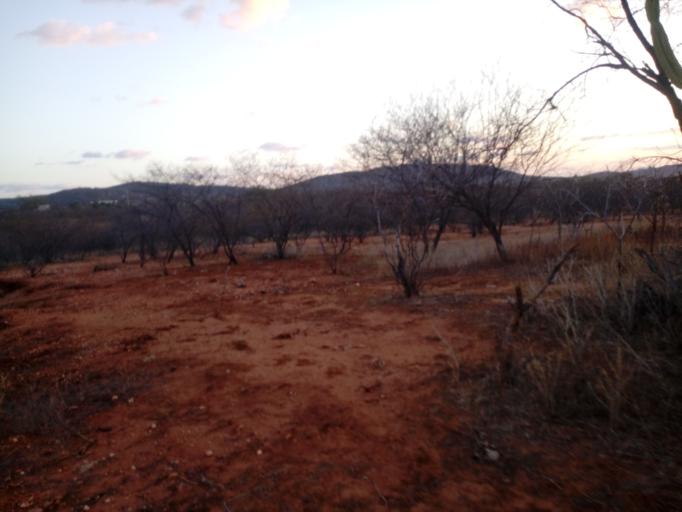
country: BR
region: Paraiba
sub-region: Patos
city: Patos
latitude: -6.8973
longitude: -37.5180
